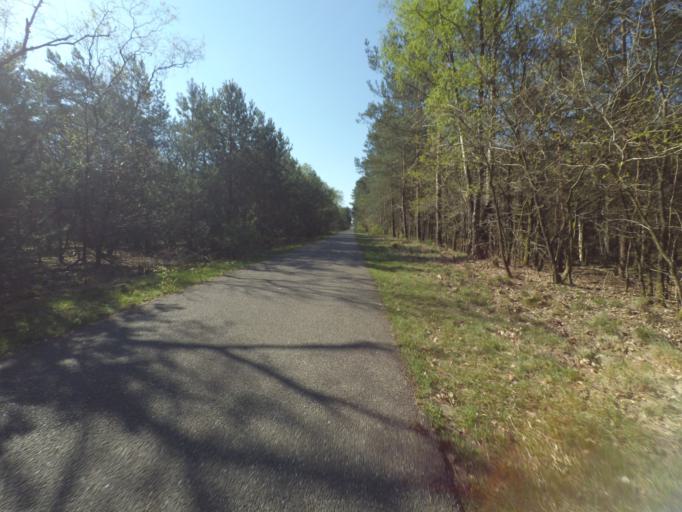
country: NL
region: Gelderland
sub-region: Gemeente Ede
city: Harskamp
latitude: 52.1811
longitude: 5.8148
